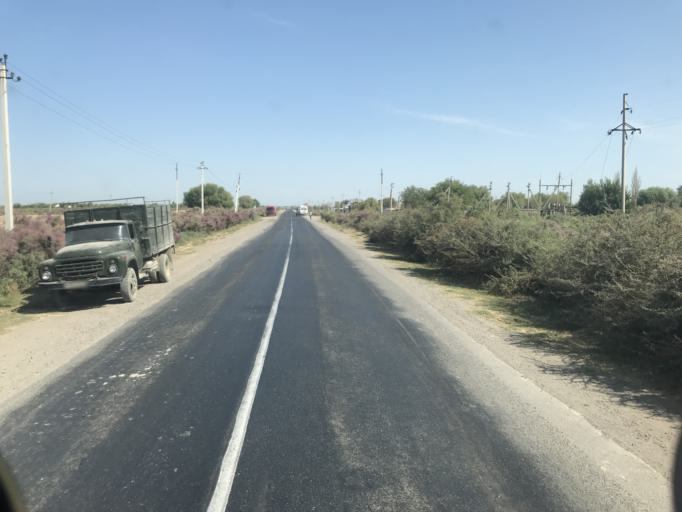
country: KZ
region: Ongtustik Qazaqstan
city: Myrzakent
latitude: 40.7285
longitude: 68.5364
